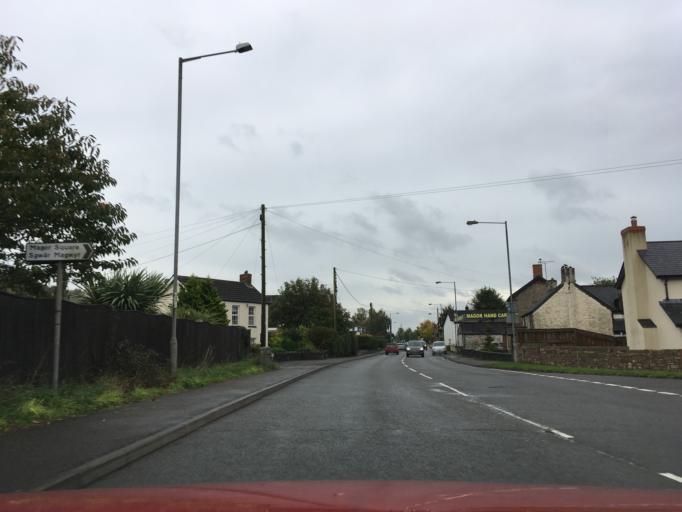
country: GB
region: Wales
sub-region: Monmouthshire
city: Magor
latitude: 51.5813
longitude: -2.8290
